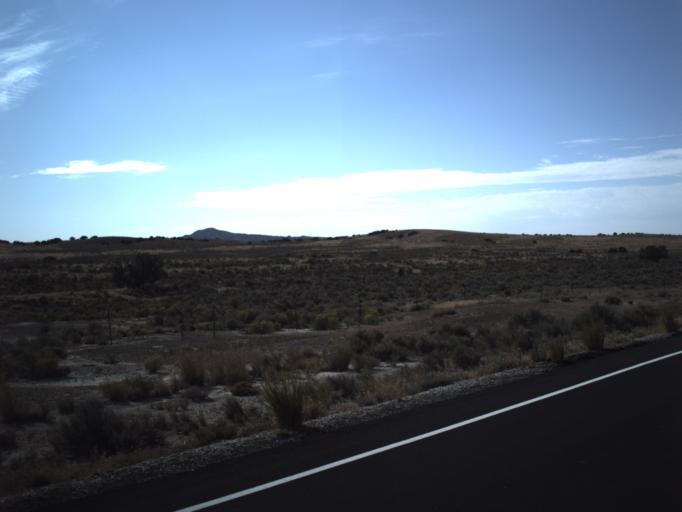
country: US
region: Idaho
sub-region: Cassia County
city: Burley
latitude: 41.6968
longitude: -113.5350
